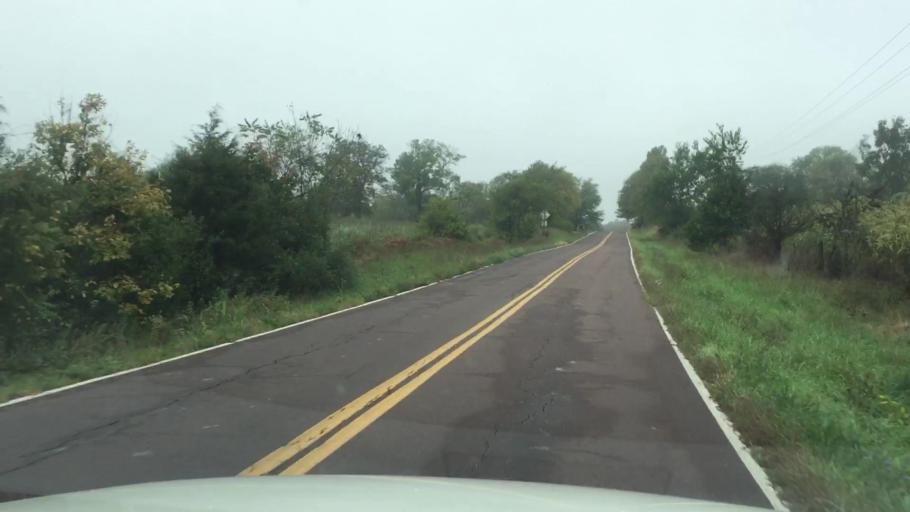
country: US
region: Missouri
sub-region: Boone County
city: Ashland
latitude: 38.8395
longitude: -92.3405
